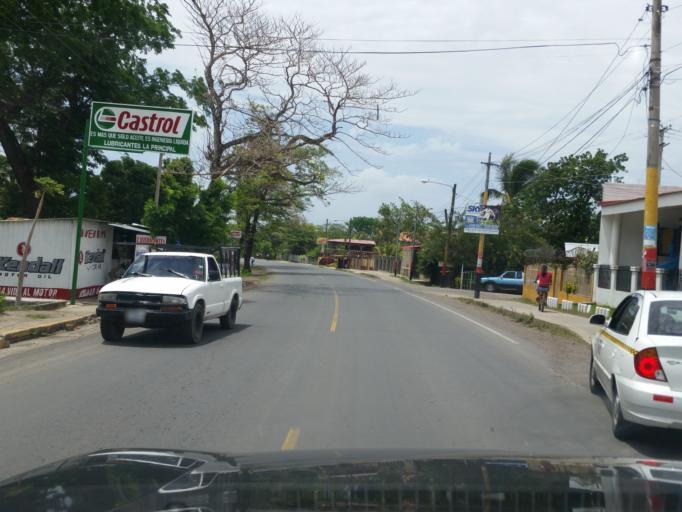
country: NI
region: Granada
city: Nandaime
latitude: 11.7563
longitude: -86.0456
